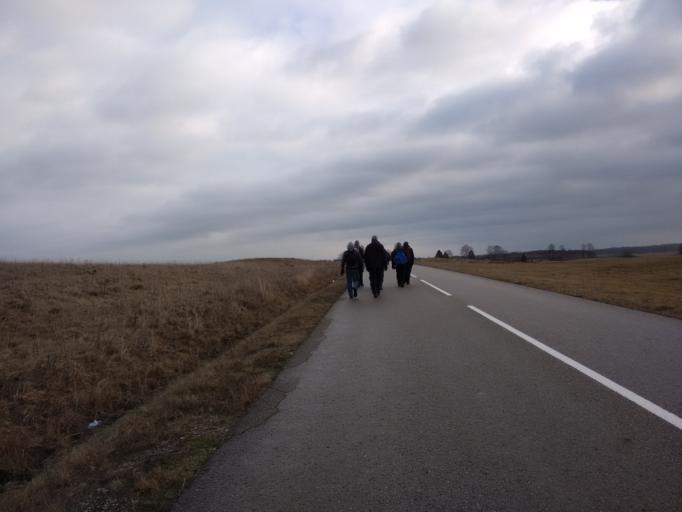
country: LT
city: Veisiejai
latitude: 54.2406
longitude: 23.8408
